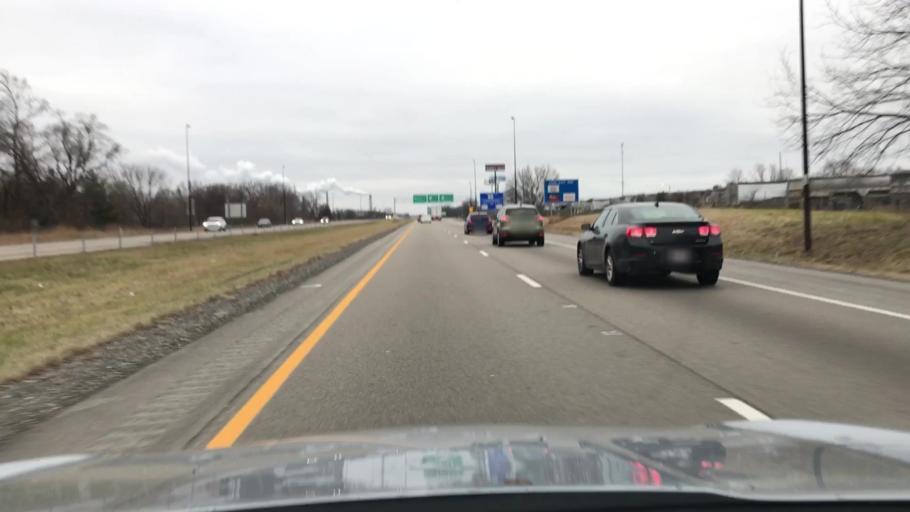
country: US
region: Illinois
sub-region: Sangamon County
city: Grandview
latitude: 39.7933
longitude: -89.5976
